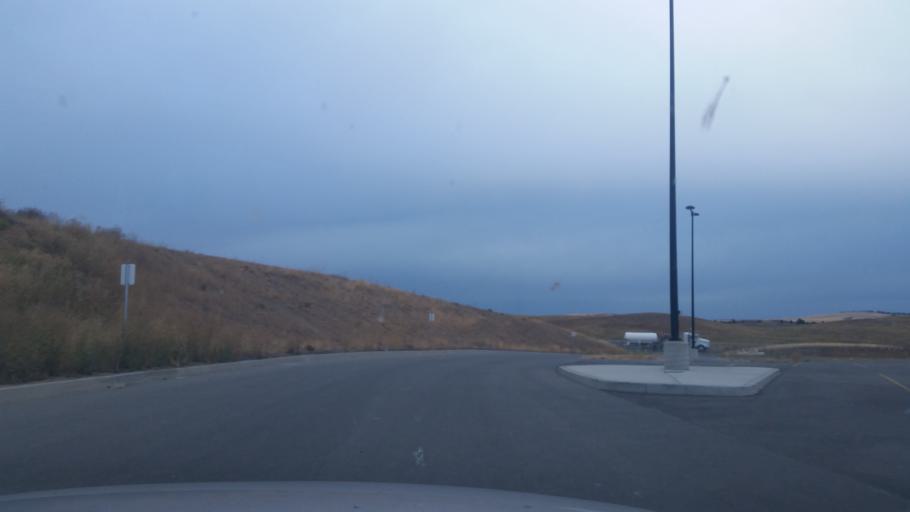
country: US
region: Washington
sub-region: Spokane County
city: Cheney
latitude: 47.4939
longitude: -117.5913
